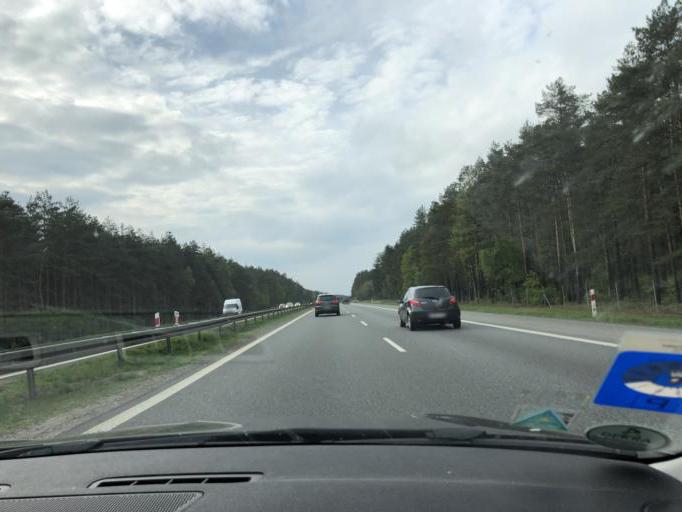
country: PL
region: Opole Voivodeship
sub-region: Powiat opolski
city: Dabrowa
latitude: 50.6258
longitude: 17.7535
